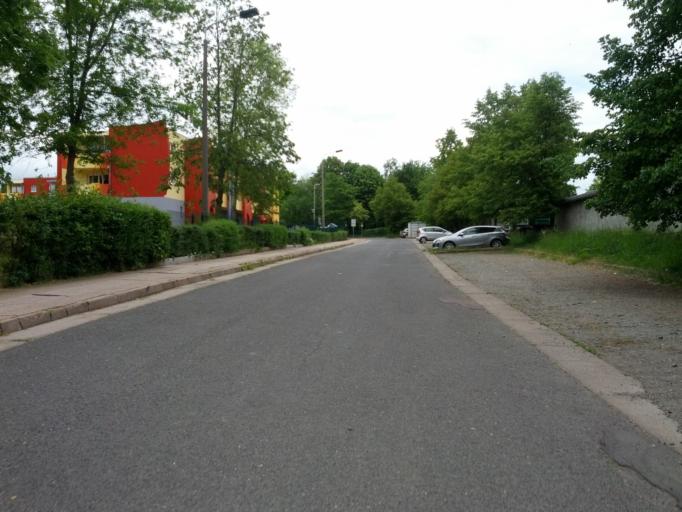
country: DE
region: Thuringia
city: Eisenach
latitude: 50.9938
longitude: 10.3116
